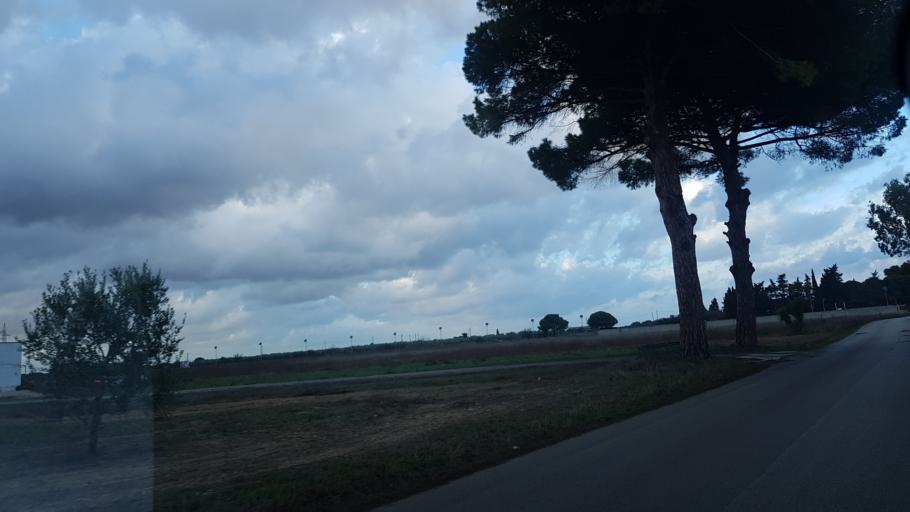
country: IT
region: Apulia
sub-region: Provincia di Brindisi
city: San Pietro Vernotico
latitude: 40.4971
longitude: 18.0028
